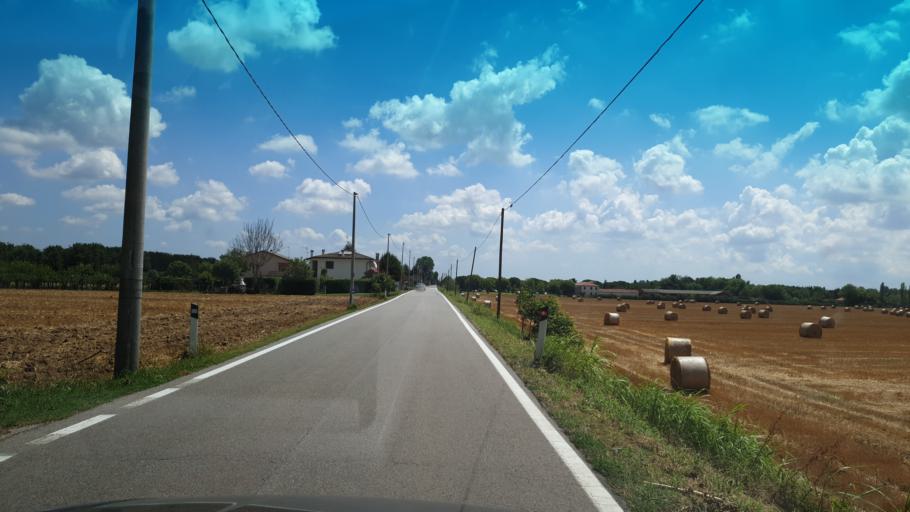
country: IT
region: Veneto
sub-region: Provincia di Rovigo
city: Mardimago
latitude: 45.1479
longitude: 11.8294
